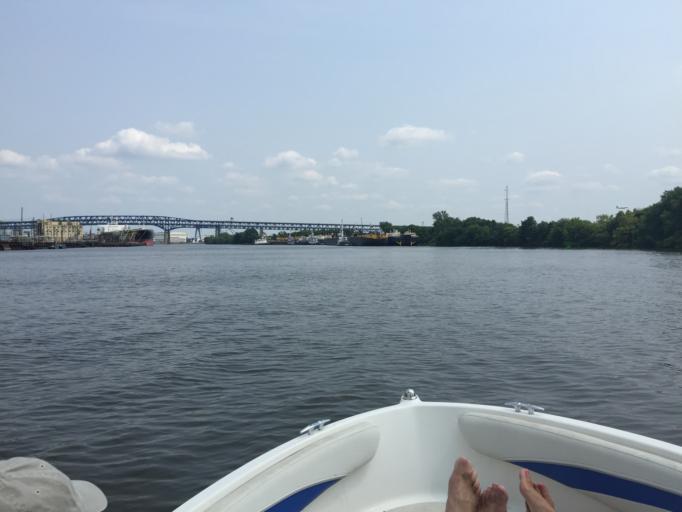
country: US
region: Pennsylvania
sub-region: Delaware County
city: Colwyn
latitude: 39.8974
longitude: -75.2113
